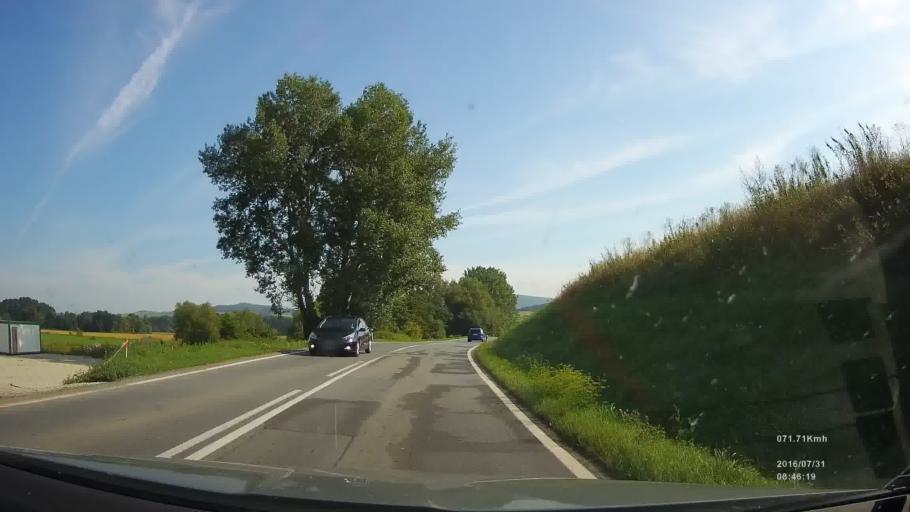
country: SK
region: Presovsky
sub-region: Okres Presov
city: Presov
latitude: 49.0535
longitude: 21.3387
